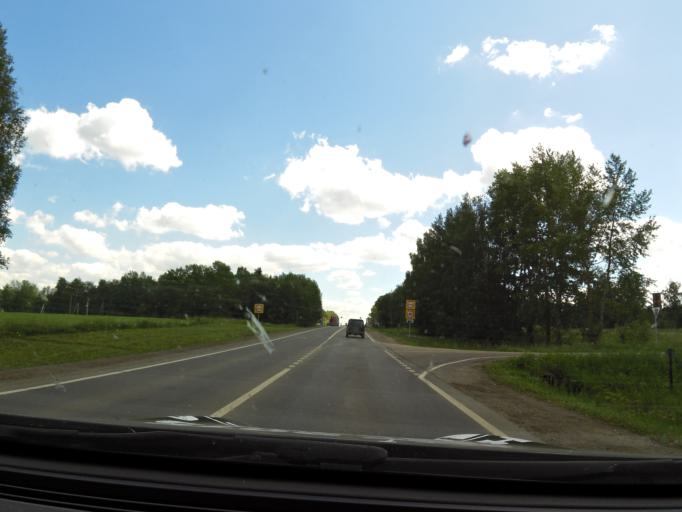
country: RU
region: Vologda
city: Molochnoye
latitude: 59.2621
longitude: 39.7452
